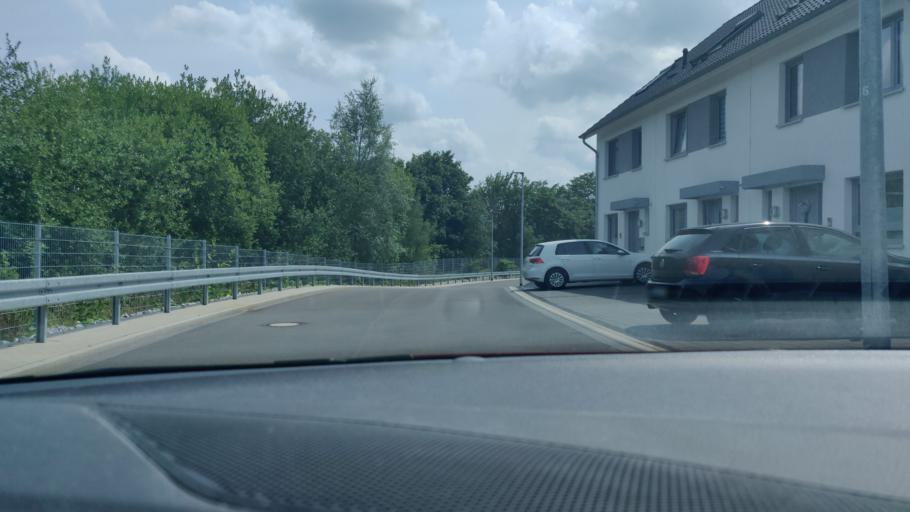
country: DE
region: North Rhine-Westphalia
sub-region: Regierungsbezirk Dusseldorf
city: Velbert
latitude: 51.3321
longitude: 7.0598
